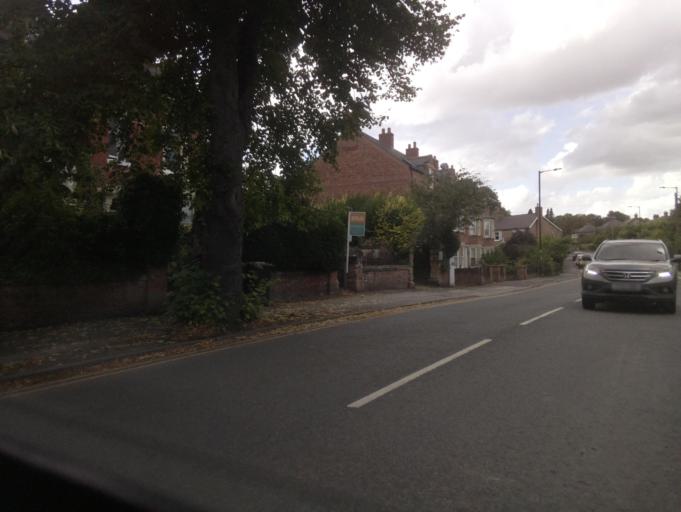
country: GB
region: England
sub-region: North Yorkshire
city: Ripon
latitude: 54.1418
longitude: -1.5231
